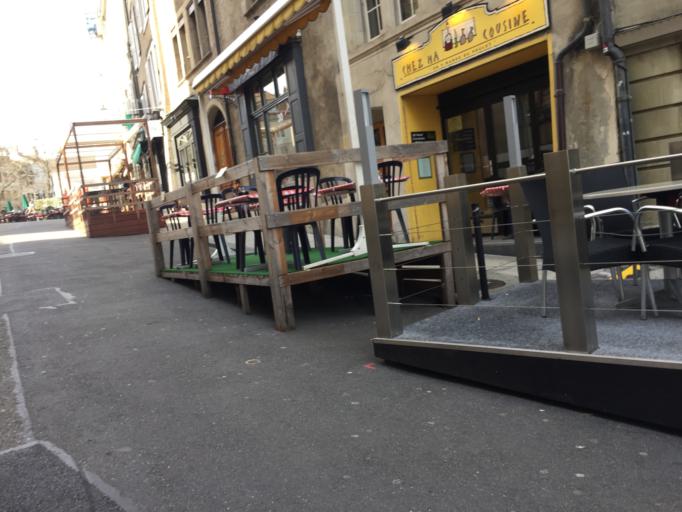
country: CH
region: Geneva
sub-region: Geneva
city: Geneve
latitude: 46.2007
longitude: 6.1494
